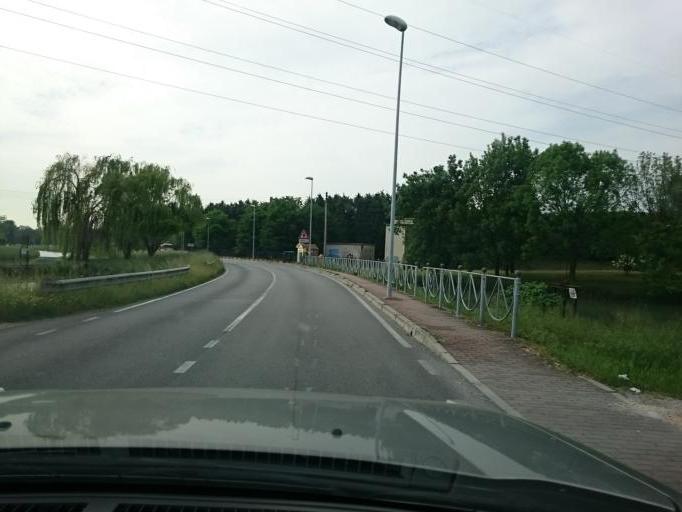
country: IT
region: Veneto
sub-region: Provincia di Venezia
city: Fornase
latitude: 45.4475
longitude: 12.1932
